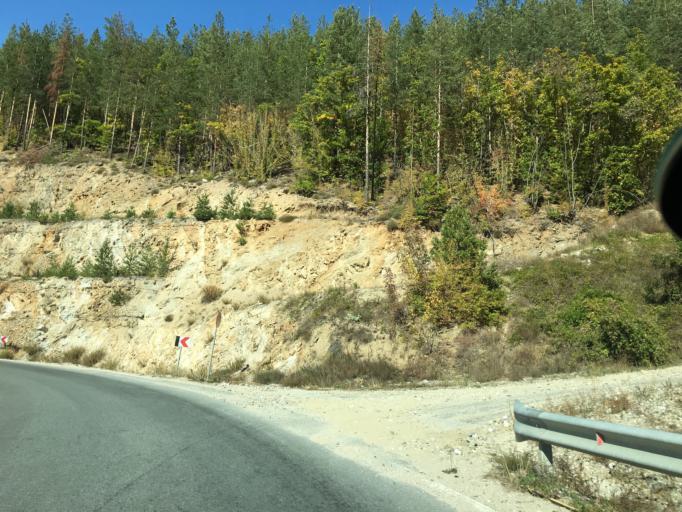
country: BG
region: Smolyan
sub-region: Obshtina Devin
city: Devin
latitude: 41.7469
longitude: 24.4374
